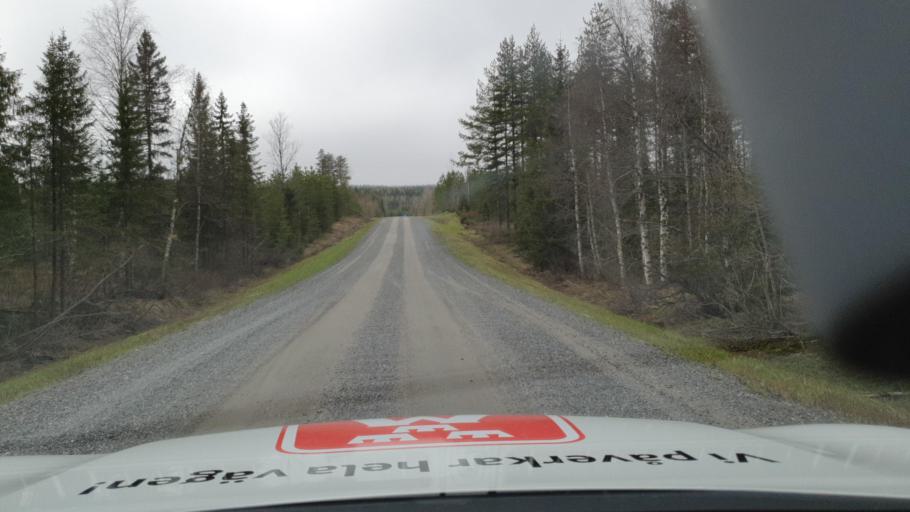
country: SE
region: Vaesterbotten
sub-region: Bjurholms Kommun
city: Bjurholm
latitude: 63.7905
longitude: 19.3149
